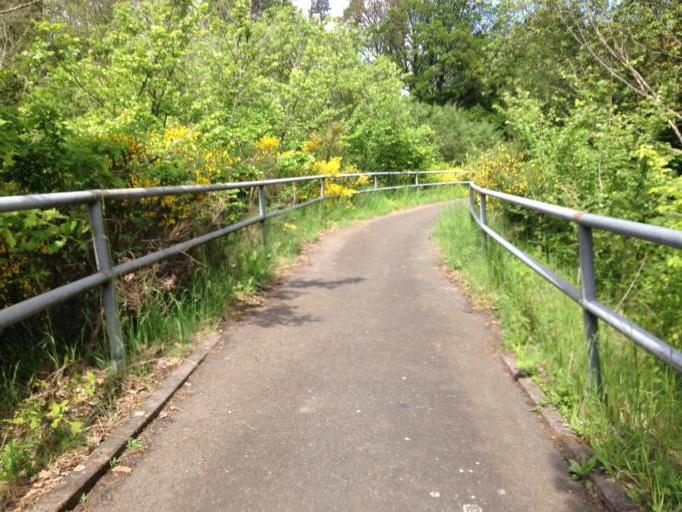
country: DE
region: Hesse
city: Lollar
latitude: 50.6331
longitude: 8.7165
